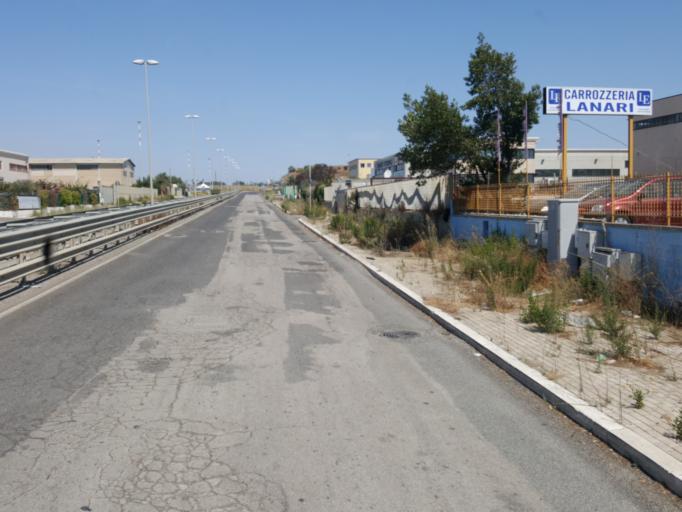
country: IT
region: Latium
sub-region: Citta metropolitana di Roma Capitale
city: Aurelia
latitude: 42.1214
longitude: 11.7784
